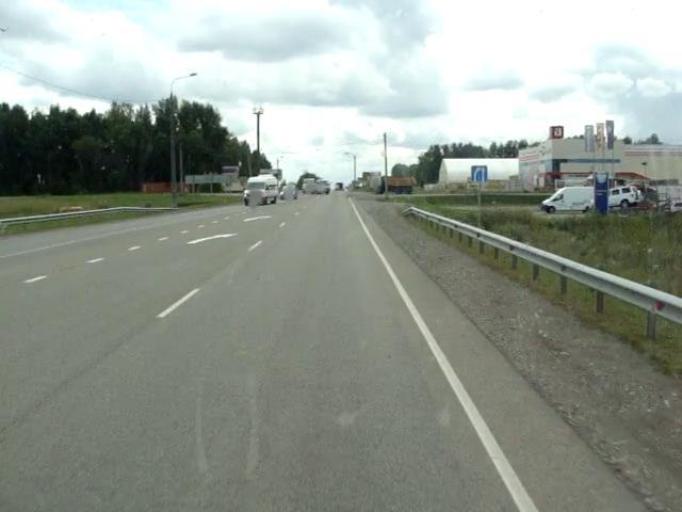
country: RU
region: Altai Krai
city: Zarya
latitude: 52.5759
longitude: 85.1798
